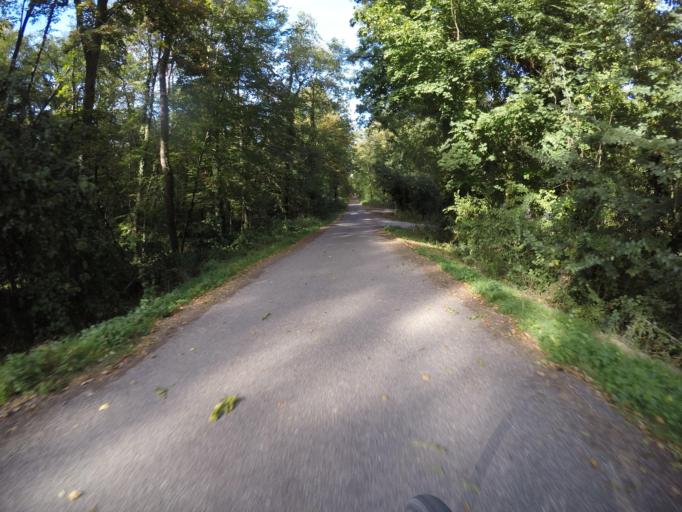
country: DE
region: Baden-Wuerttemberg
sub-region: Karlsruhe Region
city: Oftersheim
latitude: 49.3418
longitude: 8.5754
